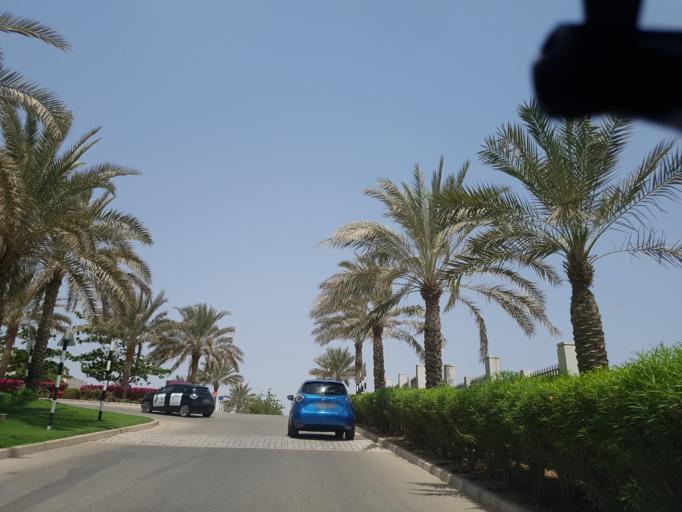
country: OM
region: Al Batinah
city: Al Liwa'
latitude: 24.4098
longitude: 56.5910
